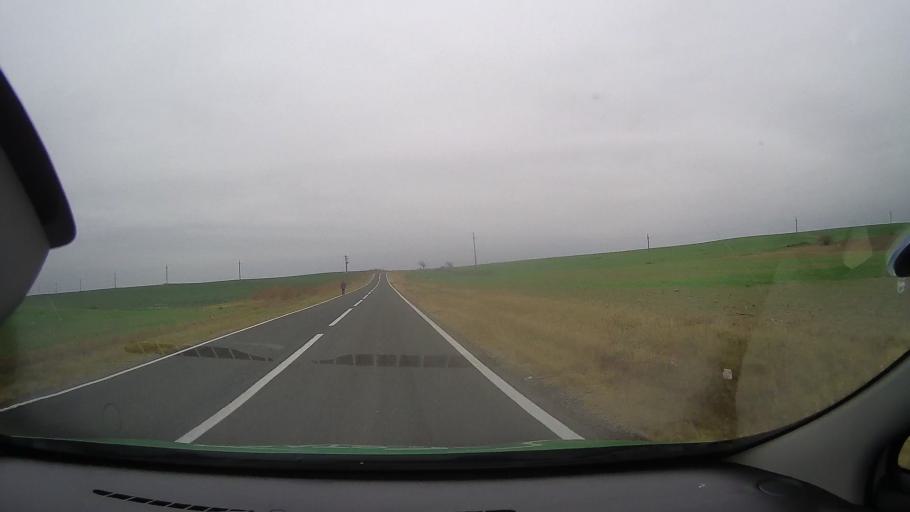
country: RO
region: Constanta
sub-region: Comuna Ghindaresti
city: Ghindaresti
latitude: 44.7052
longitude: 28.0463
